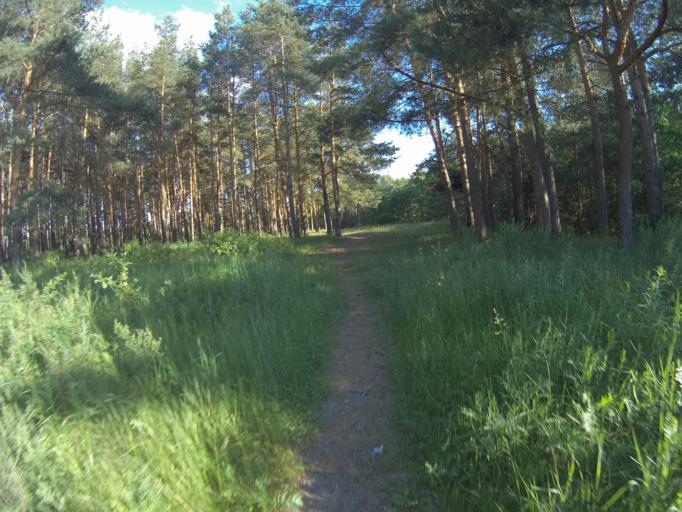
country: RU
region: Vladimir
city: Kommunar
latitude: 56.1069
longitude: 40.4299
